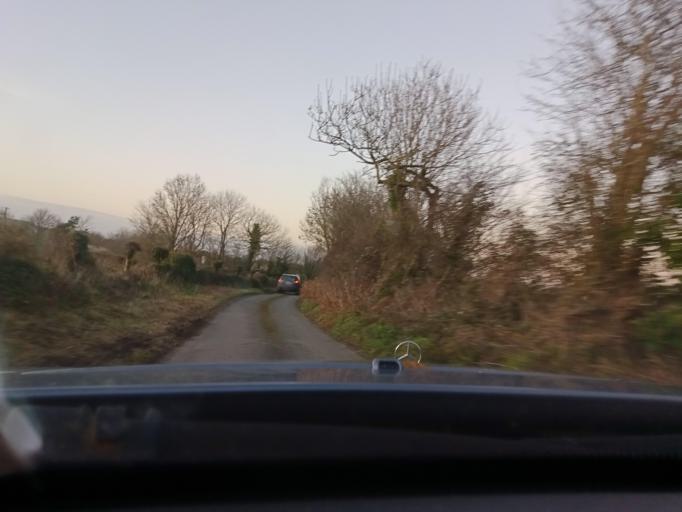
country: IE
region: Munster
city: Carrick-on-Suir
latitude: 52.4361
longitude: -7.3933
